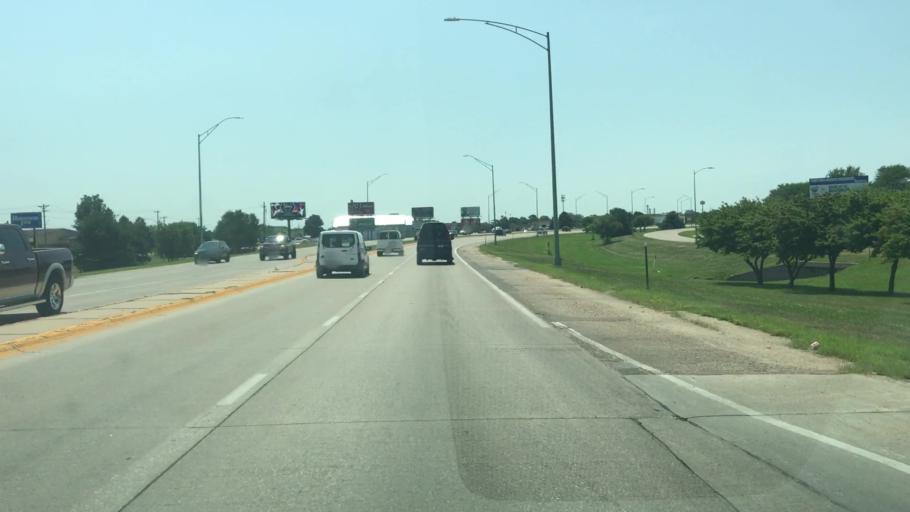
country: US
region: Nebraska
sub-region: Adams County
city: Hastings
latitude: 40.6133
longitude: -98.3833
